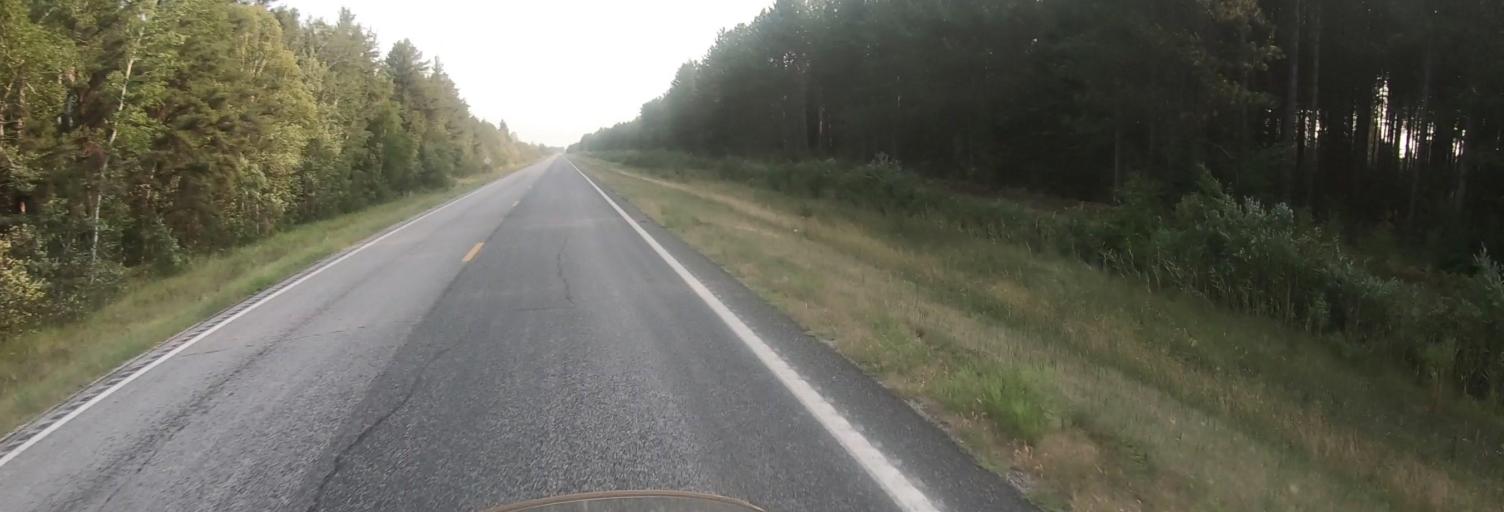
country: US
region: Minnesota
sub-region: Roseau County
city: Warroad
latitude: 48.7477
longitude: -95.3304
